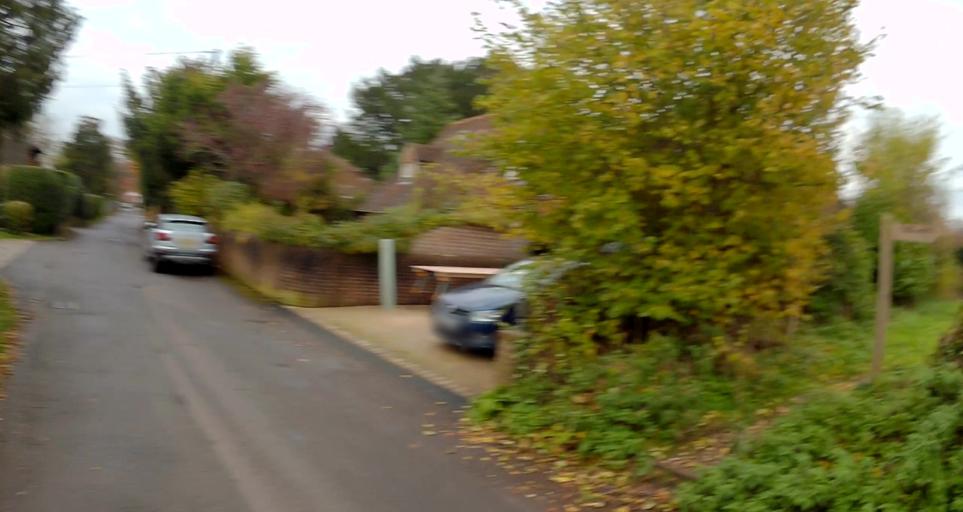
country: GB
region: England
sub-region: Hampshire
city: Fleet
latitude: 51.2318
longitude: -0.8661
